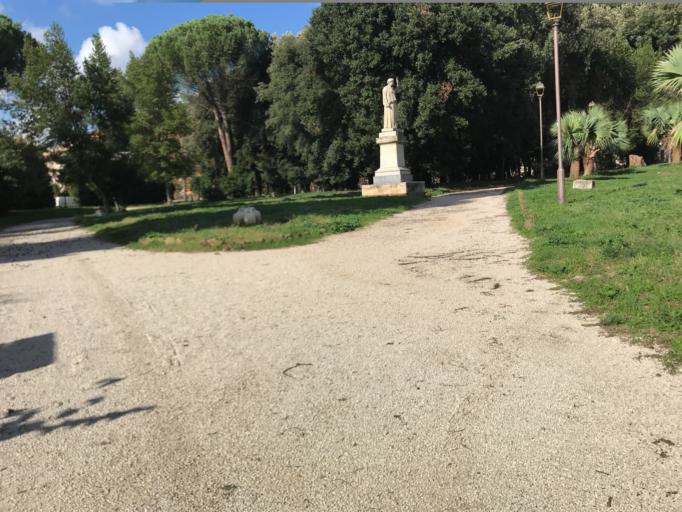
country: IT
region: Latium
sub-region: Citta metropolitana di Roma Capitale
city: Rome
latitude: 41.9138
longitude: 12.5105
